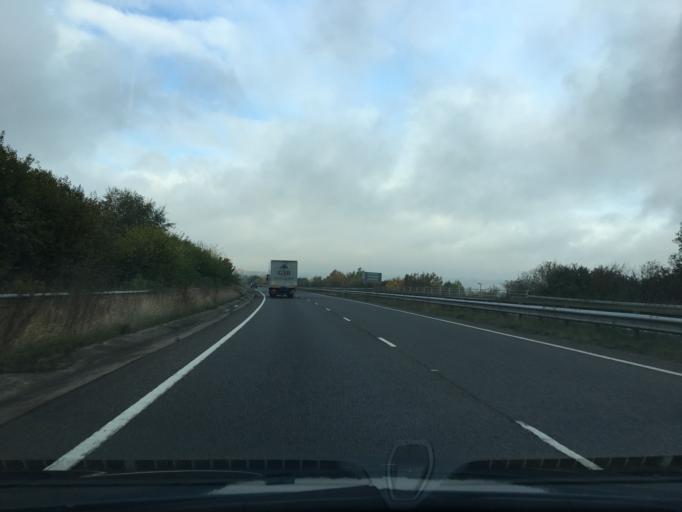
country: GB
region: England
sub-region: Surrey
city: Seale
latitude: 51.2275
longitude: -0.7414
